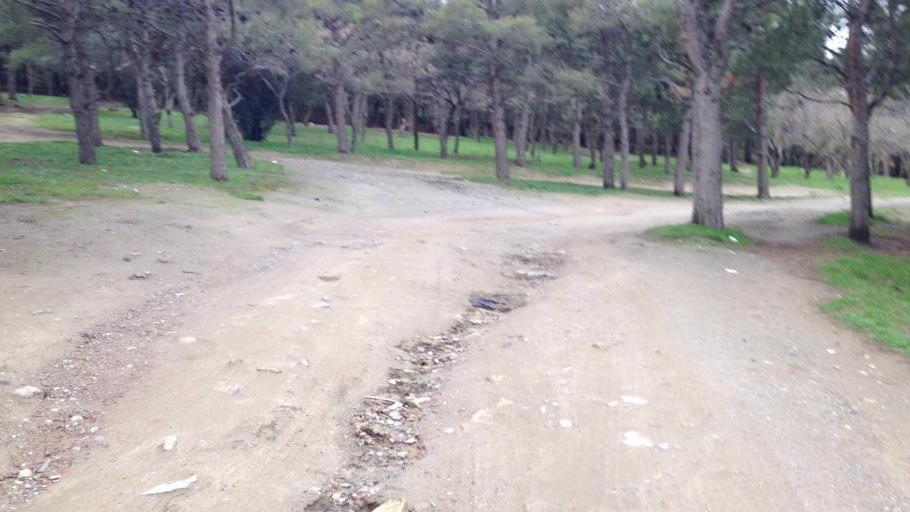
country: AZ
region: Baki
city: Baku
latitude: 40.3937
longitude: 49.8520
